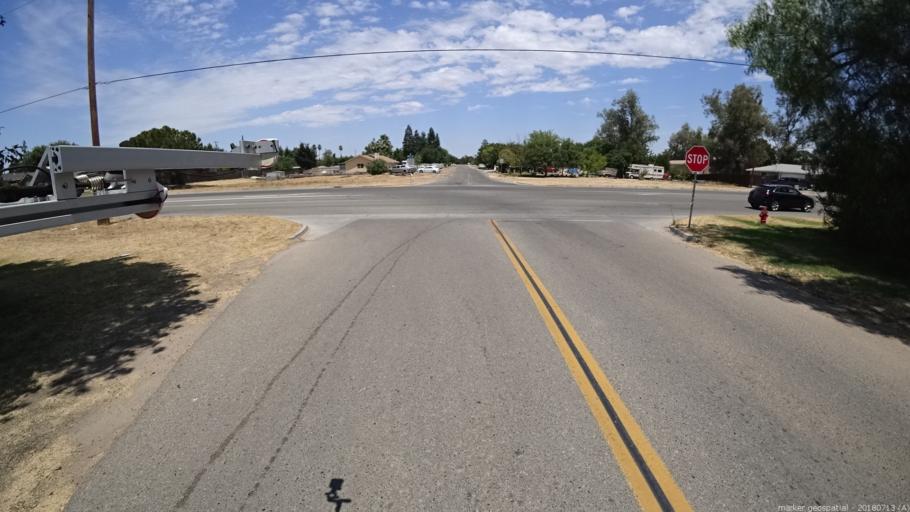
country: US
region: California
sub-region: Madera County
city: Madera Acres
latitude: 36.9962
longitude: -120.0805
